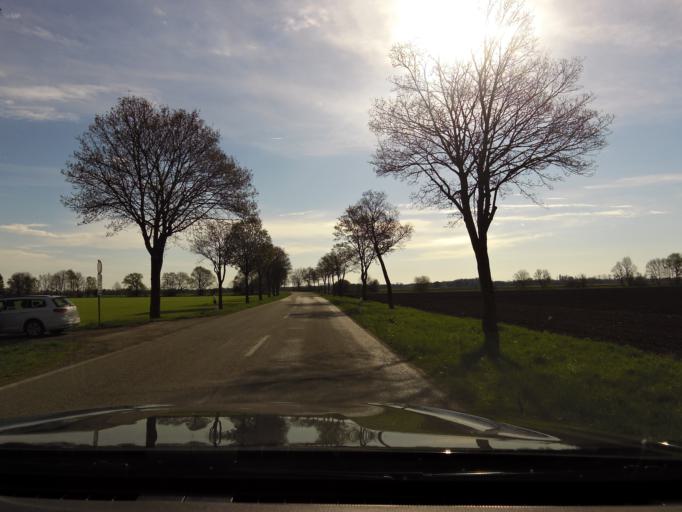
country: DE
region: Bavaria
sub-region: Upper Bavaria
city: Hallbergmoos
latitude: 48.3341
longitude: 11.7669
